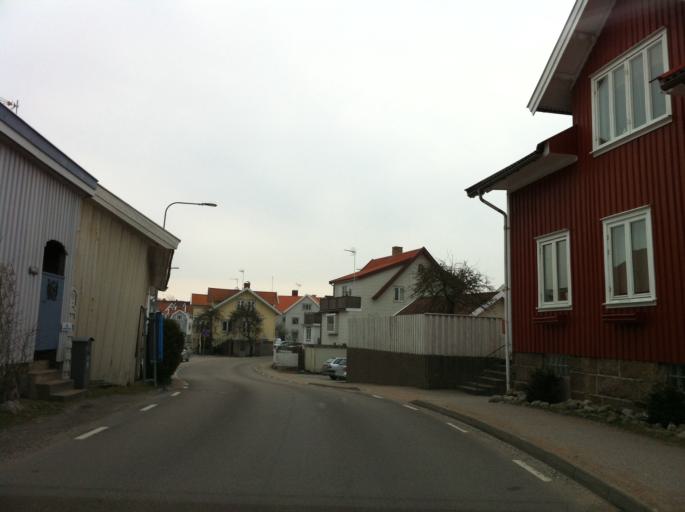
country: SE
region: Vaestra Goetaland
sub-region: Orust
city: Henan
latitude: 58.1645
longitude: 11.7048
